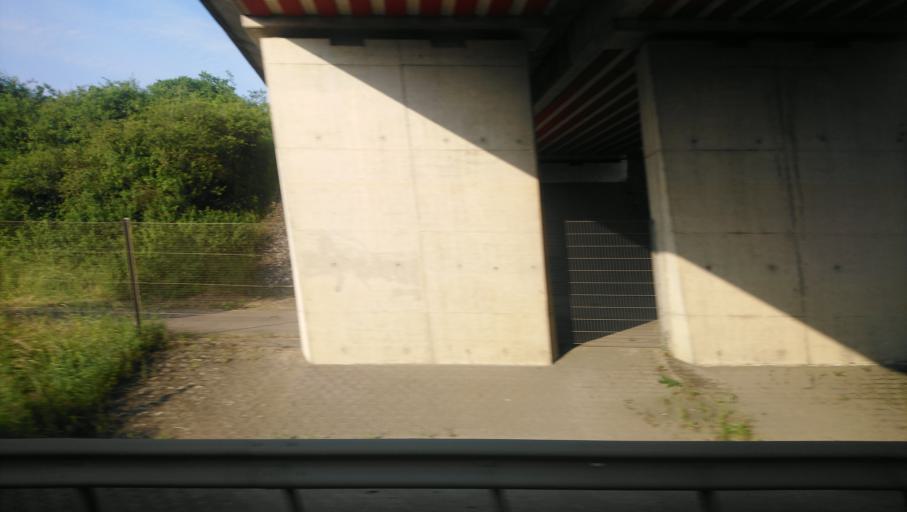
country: LU
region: Luxembourg
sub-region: Canton d'Esch-sur-Alzette
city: Kayl
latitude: 49.5038
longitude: 6.0420
